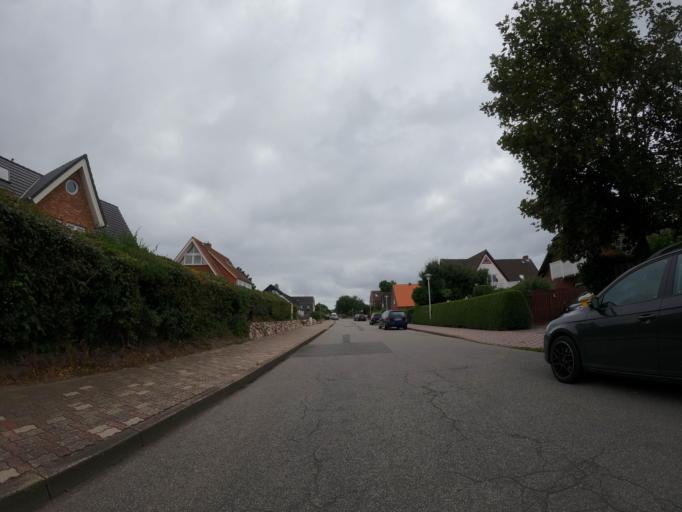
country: DE
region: Schleswig-Holstein
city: Westerland
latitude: 54.9169
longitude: 8.3168
